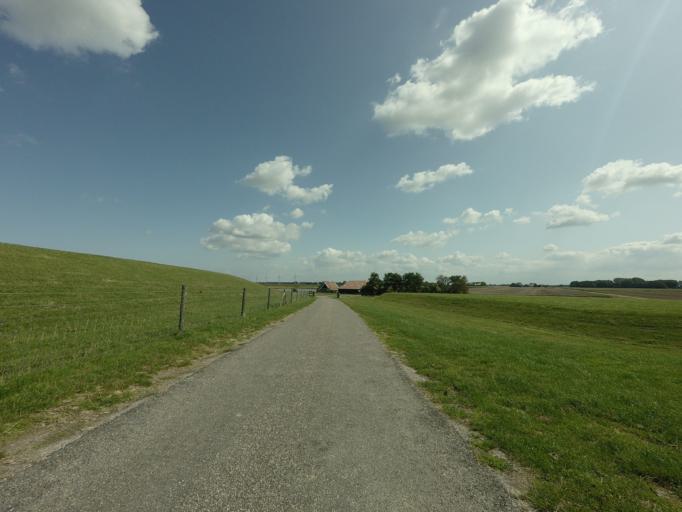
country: NL
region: Friesland
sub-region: Gemeente Ferwerderadiel
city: Hallum
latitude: 53.3195
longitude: 5.7549
